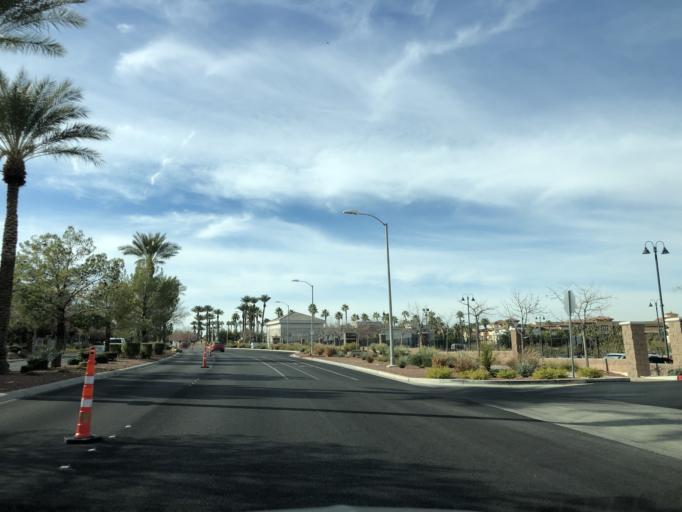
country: US
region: Nevada
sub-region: Clark County
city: Whitney
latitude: 36.0202
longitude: -115.0851
